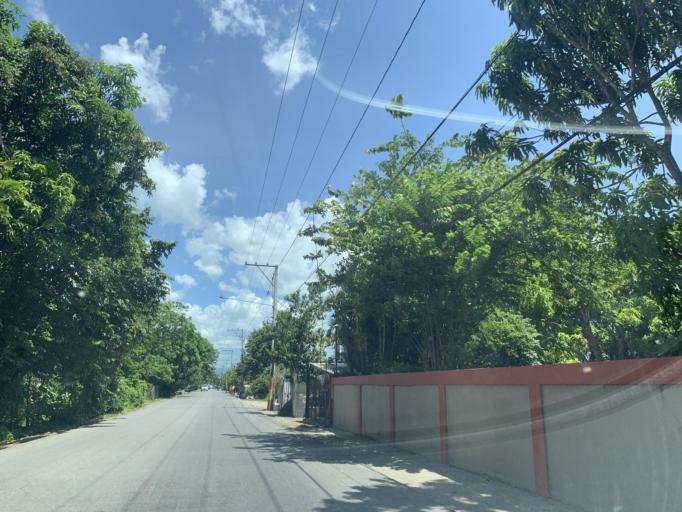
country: DO
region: Puerto Plata
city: Cabarete
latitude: 19.6978
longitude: -70.3820
